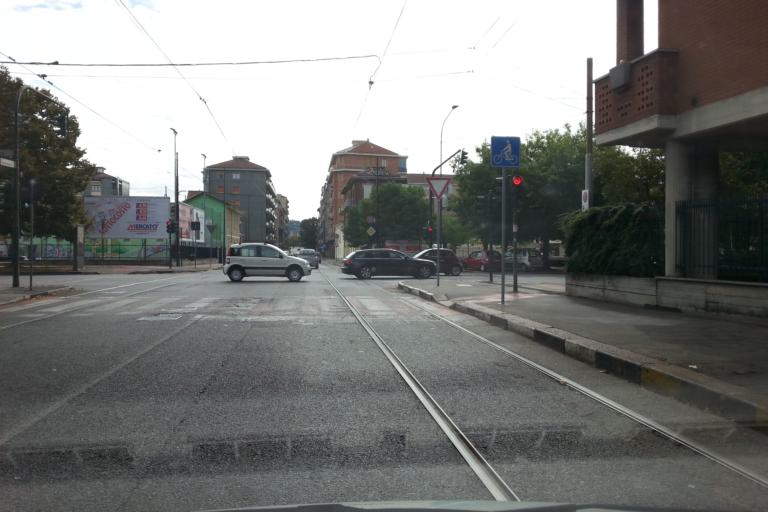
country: IT
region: Piedmont
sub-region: Provincia di Torino
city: Nichelino
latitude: 45.0251
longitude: 7.6519
